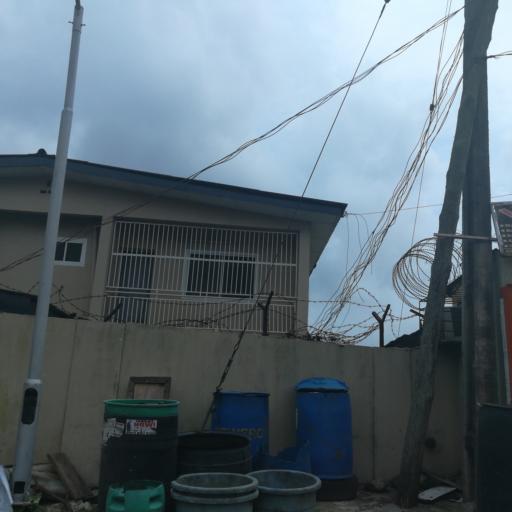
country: NG
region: Lagos
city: Ojota
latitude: 6.5773
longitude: 3.3899
